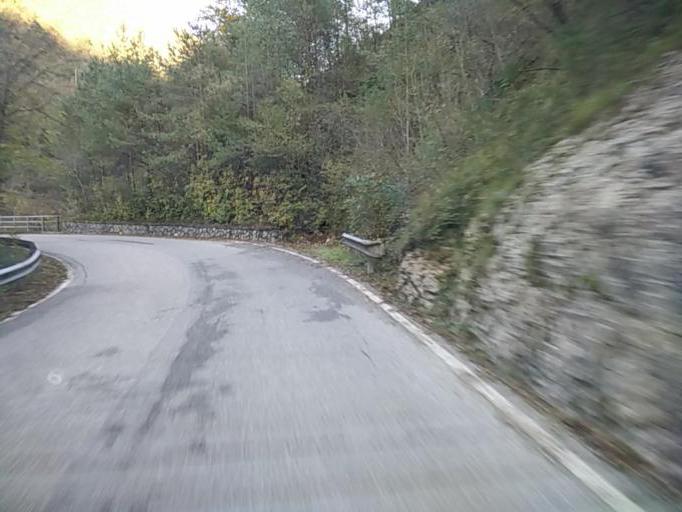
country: IT
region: Lombardy
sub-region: Provincia di Brescia
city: Gargnano
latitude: 45.7046
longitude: 10.6165
